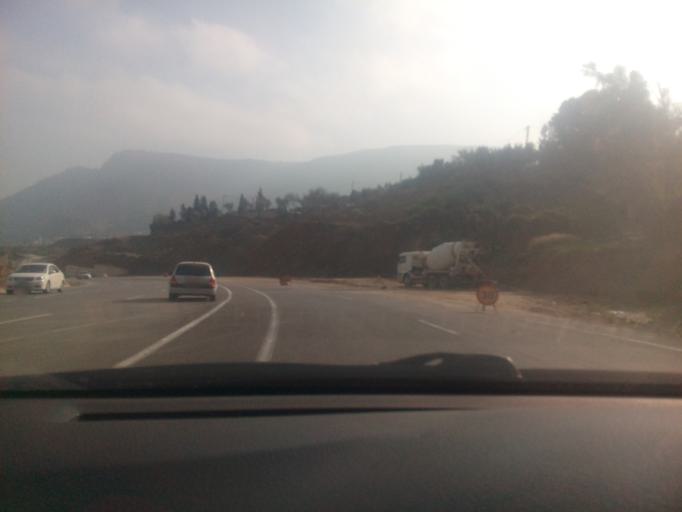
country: DZ
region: Oran
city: Mers el Kebir
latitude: 35.7134
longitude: -0.6989
